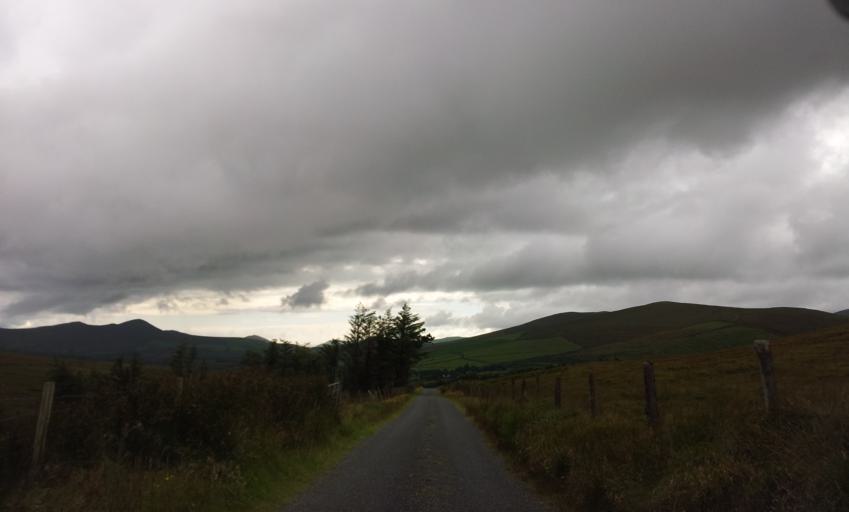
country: IE
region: Munster
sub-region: Ciarrai
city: Killorglin
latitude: 52.1958
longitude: -9.9236
